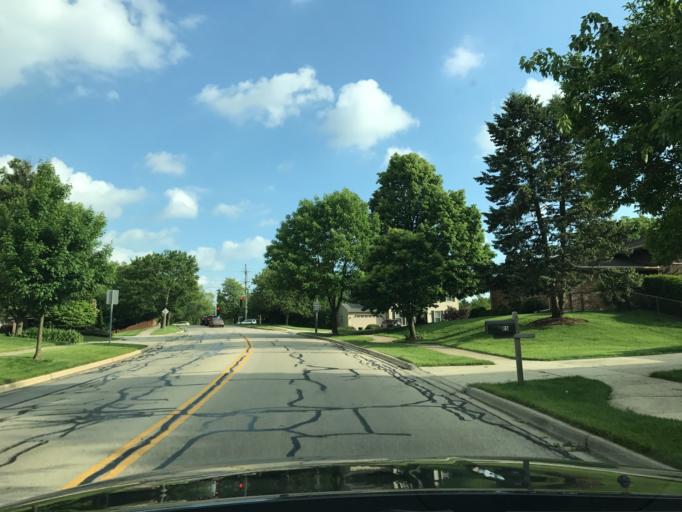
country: US
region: Illinois
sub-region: DuPage County
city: Naperville
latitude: 41.7757
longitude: -88.1295
